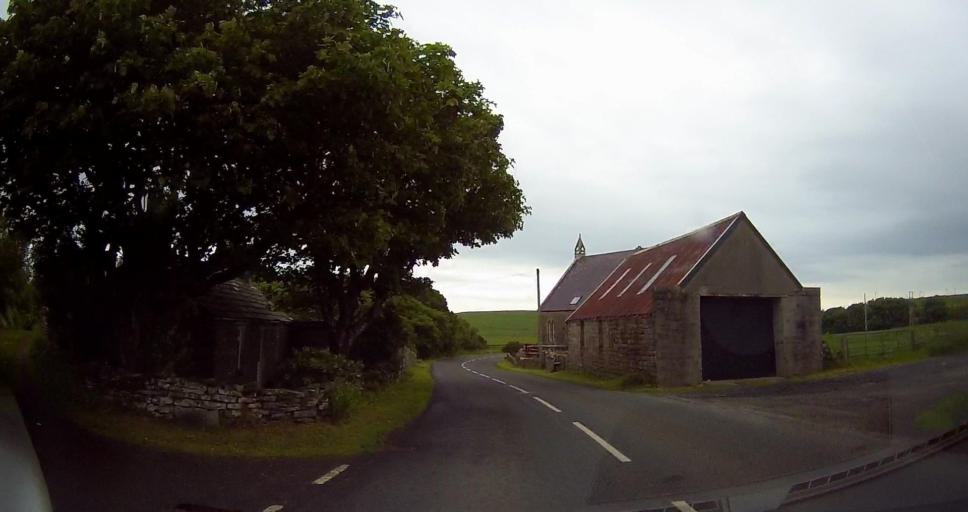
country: GB
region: Scotland
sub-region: Orkney Islands
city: Orkney
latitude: 59.1133
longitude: -3.1077
